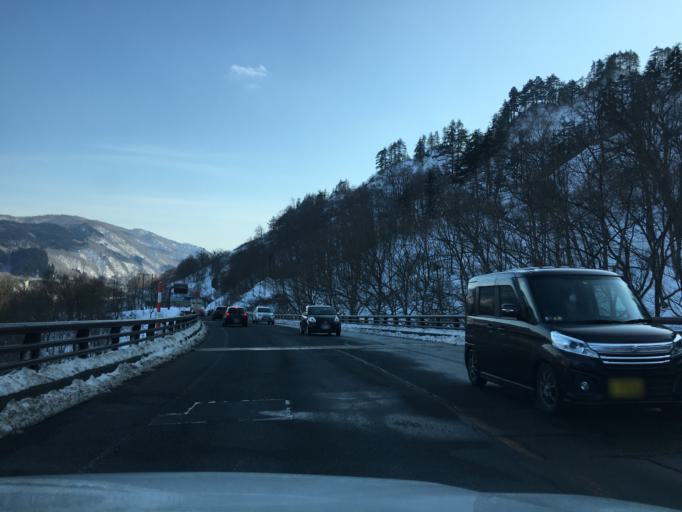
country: JP
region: Yamagata
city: Sagae
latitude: 38.4592
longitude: 139.9905
